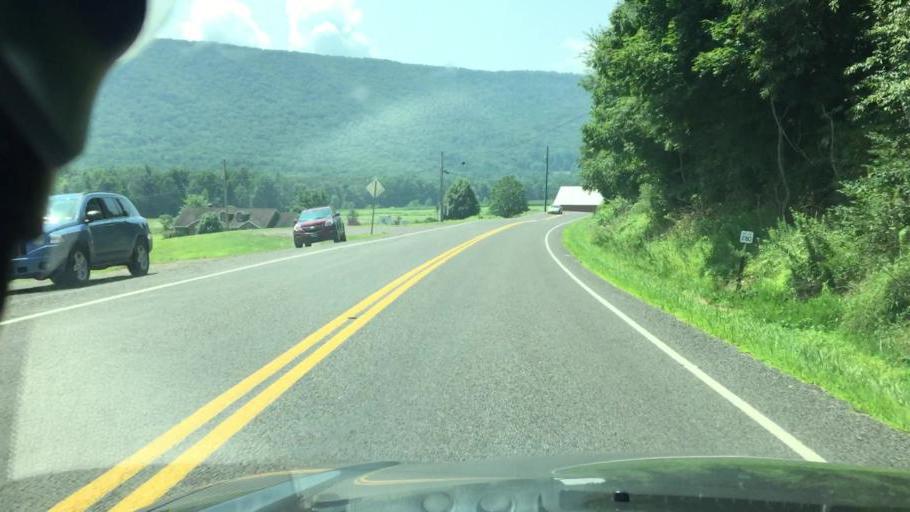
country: US
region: Pennsylvania
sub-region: Columbia County
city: Mifflinville
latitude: 41.0037
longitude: -76.3222
